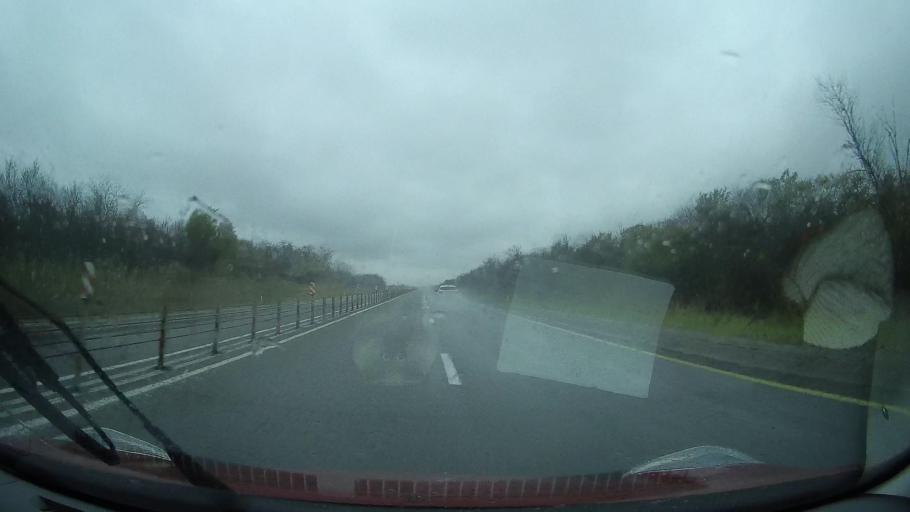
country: RU
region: Stavropol'skiy
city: Nevinnomyssk
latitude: 44.6386
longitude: 41.9808
